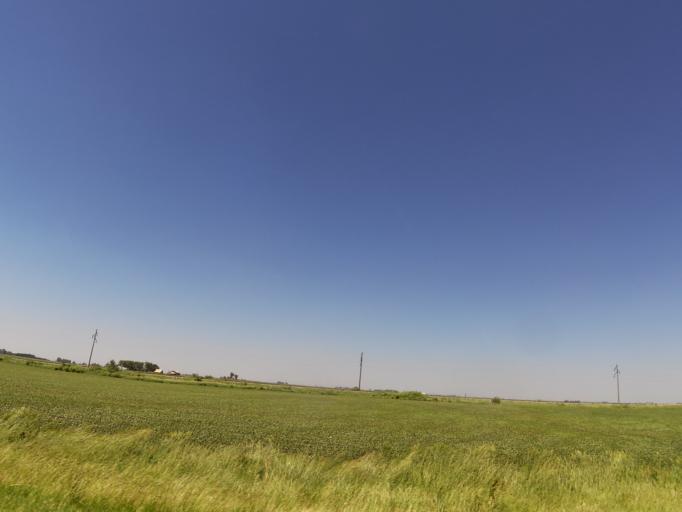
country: US
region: Illinois
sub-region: Woodford County
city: El Paso
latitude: 40.7386
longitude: -88.9535
